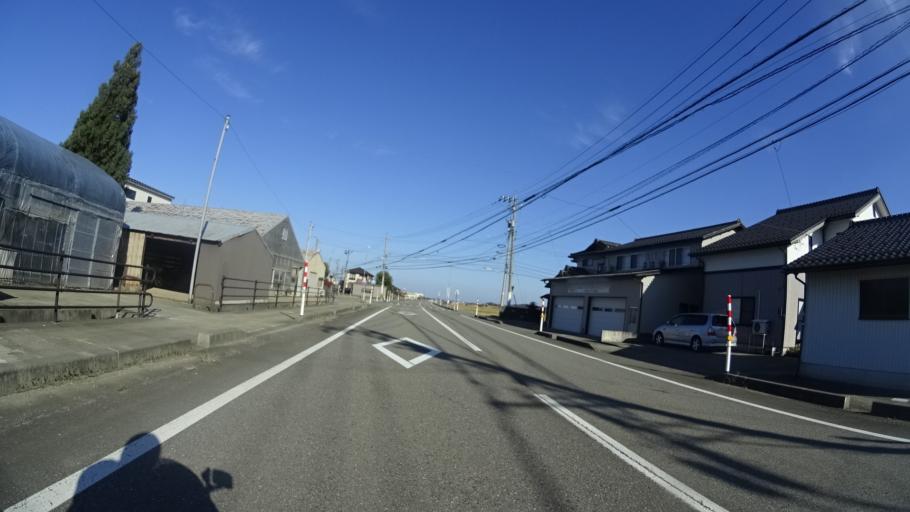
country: JP
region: Ishikawa
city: Komatsu
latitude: 36.2861
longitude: 136.3903
